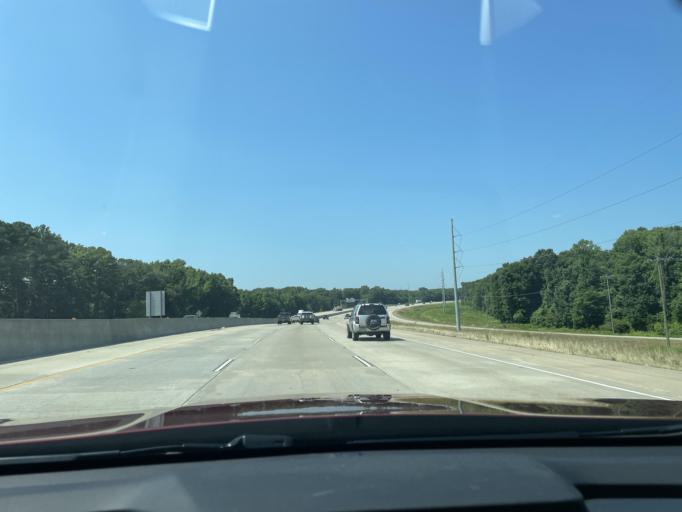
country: US
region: Arkansas
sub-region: Pulaski County
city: Jacksonville
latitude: 34.8610
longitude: -92.1303
